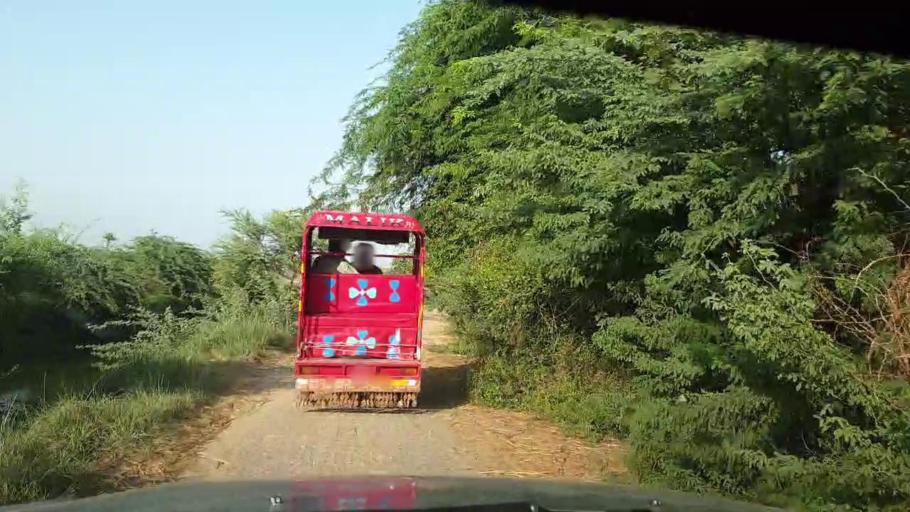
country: PK
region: Sindh
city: Rajo Khanani
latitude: 25.0150
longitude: 68.7610
